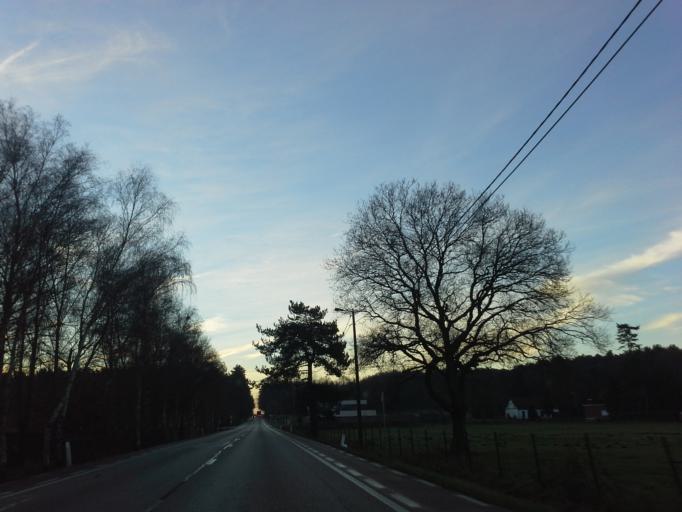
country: BE
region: Flanders
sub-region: Provincie Antwerpen
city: Laakdal
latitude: 51.0614
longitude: 5.0432
